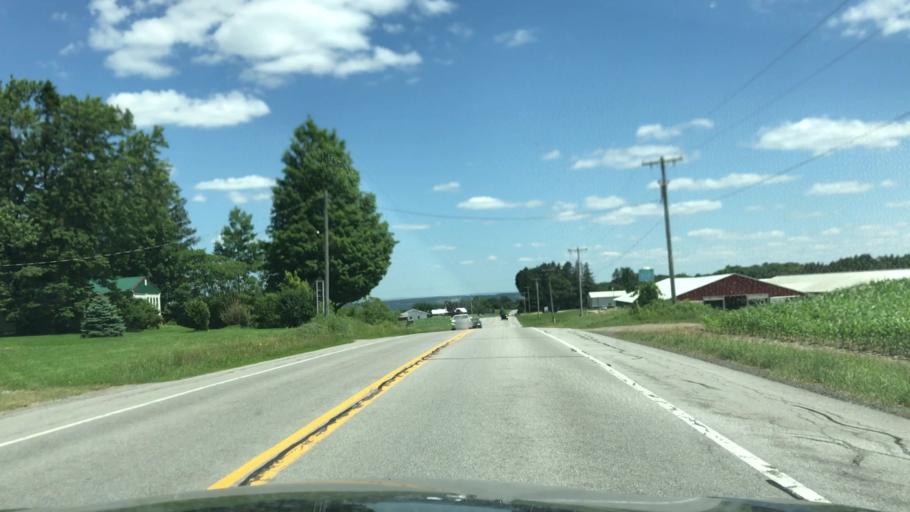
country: US
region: New York
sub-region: Wyoming County
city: Warsaw
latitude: 42.7455
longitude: -78.2213
